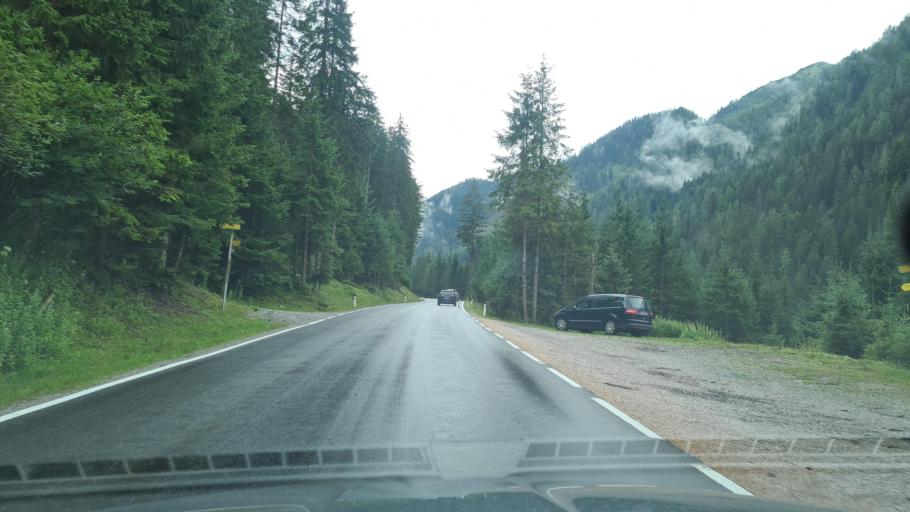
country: AT
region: Salzburg
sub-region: Politischer Bezirk Sankt Johann im Pongau
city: Radstadt
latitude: 47.3288
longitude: 13.4454
